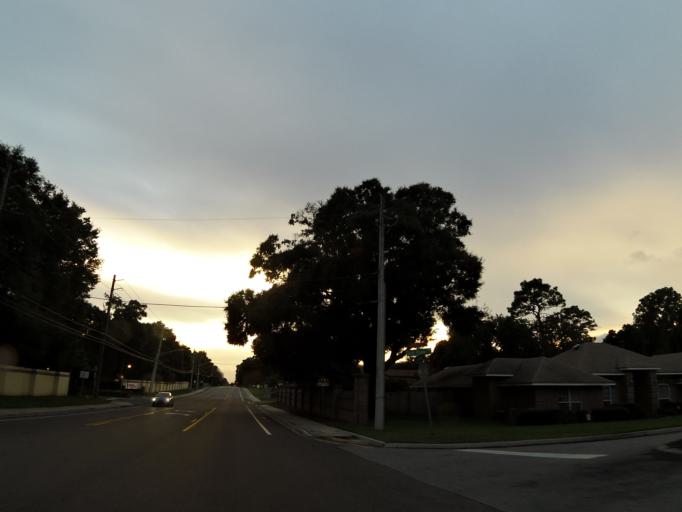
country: US
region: Florida
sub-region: Duval County
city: Jacksonville
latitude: 30.3668
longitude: -81.5695
